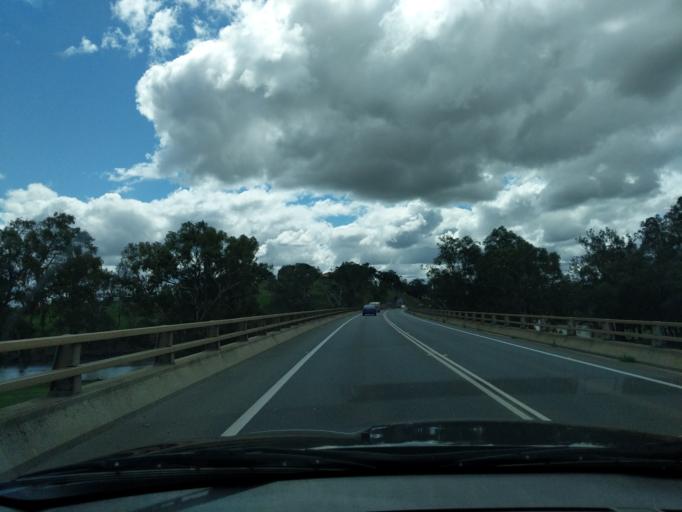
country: AU
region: New South Wales
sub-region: Wagga Wagga
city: Wagga Wagga
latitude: -35.0910
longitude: 147.3476
